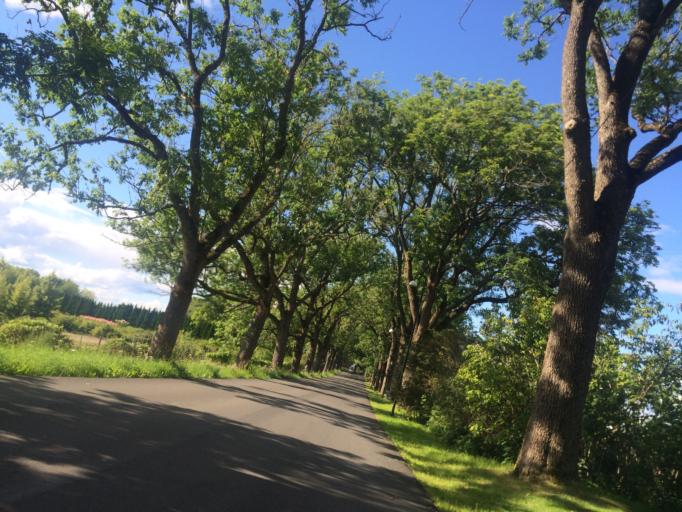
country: NO
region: Akershus
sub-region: As
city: As
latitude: 59.6694
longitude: 10.7707
